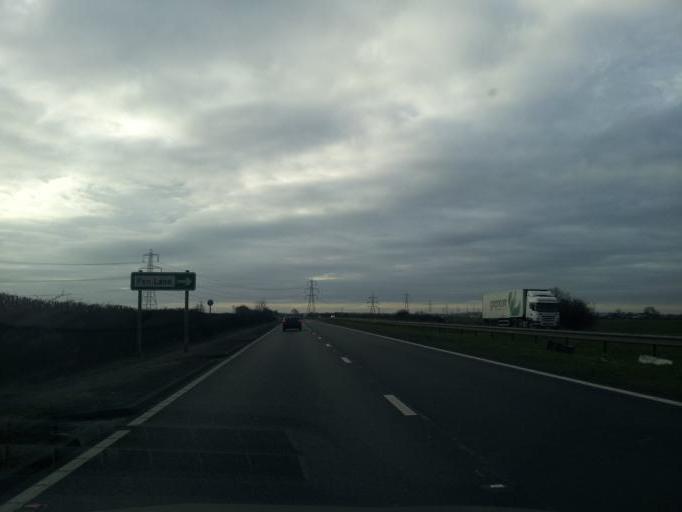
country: GB
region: England
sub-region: Lincolnshire
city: Long Bennington
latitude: 53.0218
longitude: -0.7673
